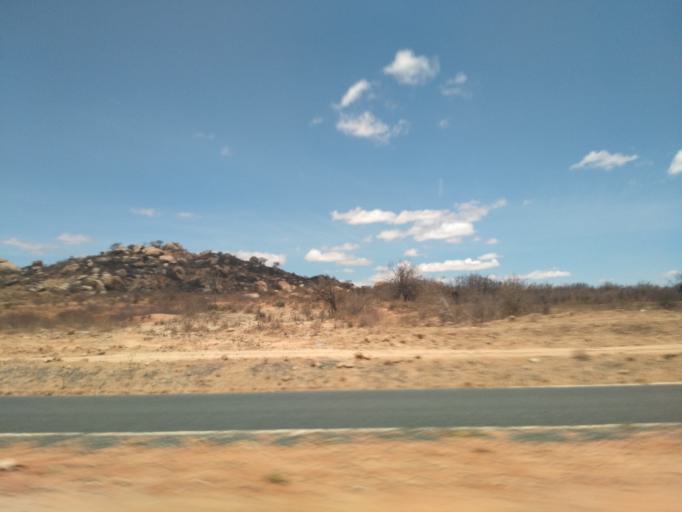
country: TZ
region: Dodoma
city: Kisasa
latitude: -6.1810
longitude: 35.8380
